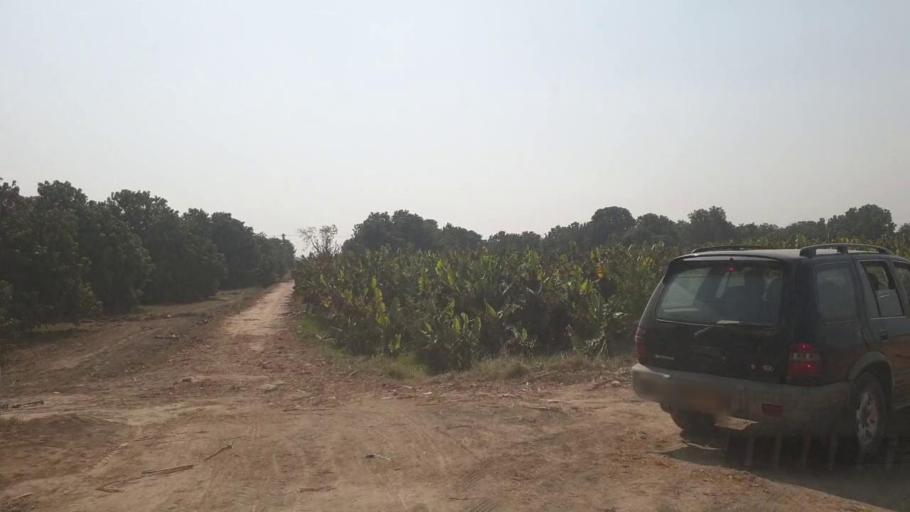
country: PK
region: Sindh
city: Tando Allahyar
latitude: 25.4577
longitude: 68.7989
